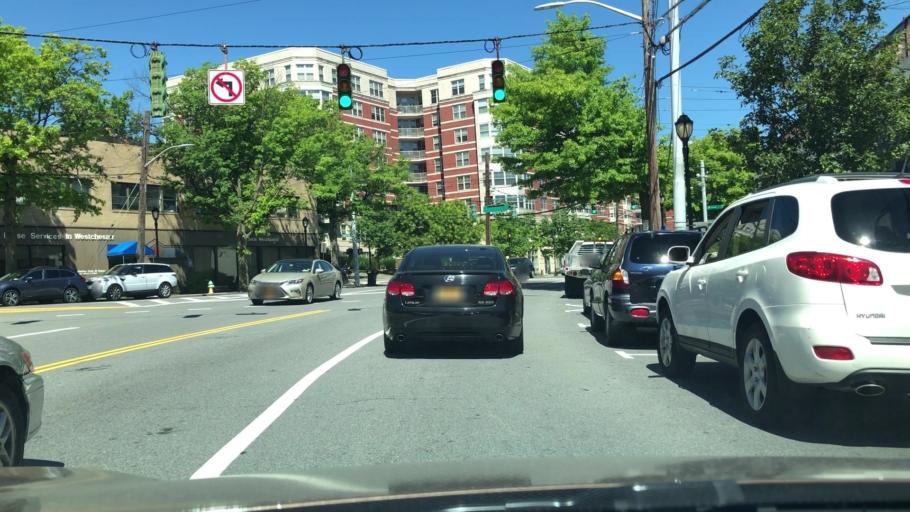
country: US
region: New York
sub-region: Westchester County
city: White Plains
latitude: 41.0240
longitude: -73.7626
